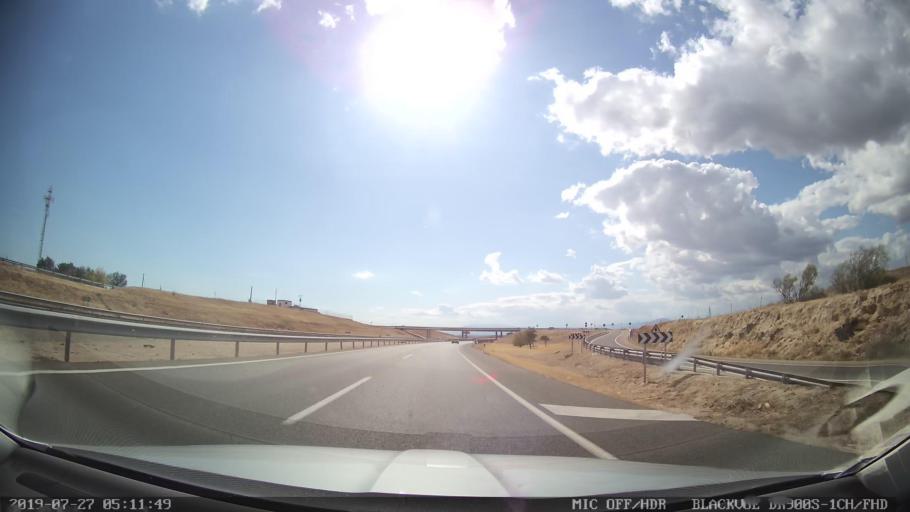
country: ES
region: Castille-La Mancha
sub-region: Province of Toledo
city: Quismondo
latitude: 40.1135
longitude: -4.3103
